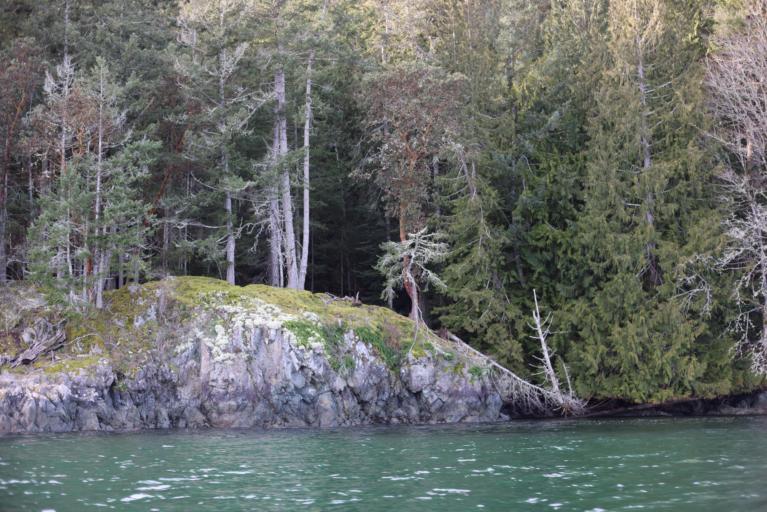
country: CA
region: British Columbia
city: Duncan
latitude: 48.7582
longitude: -123.5760
